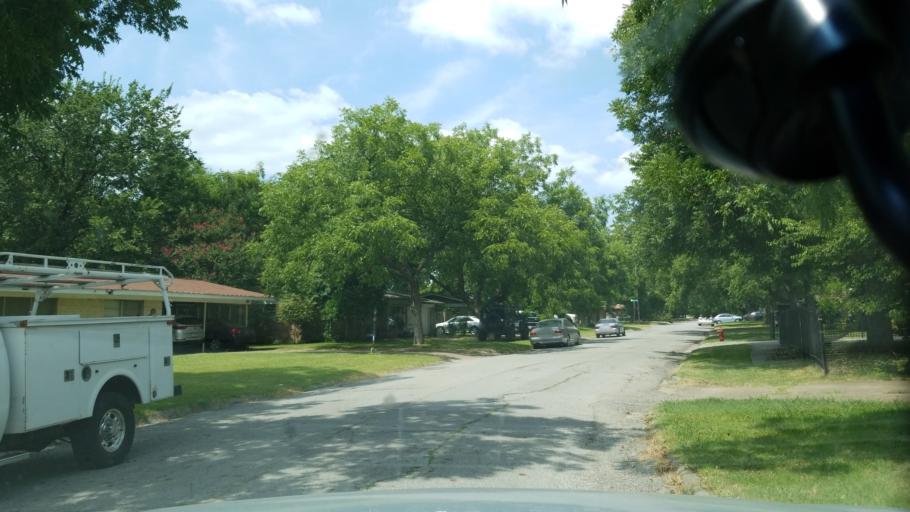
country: US
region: Texas
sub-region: Dallas County
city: Grand Prairie
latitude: 32.7543
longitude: -96.9873
